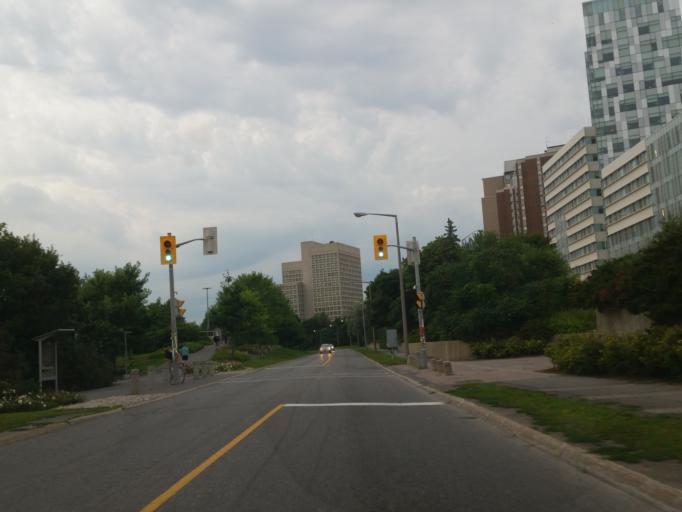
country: CA
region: Ontario
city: Ottawa
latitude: 45.4203
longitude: -75.6828
